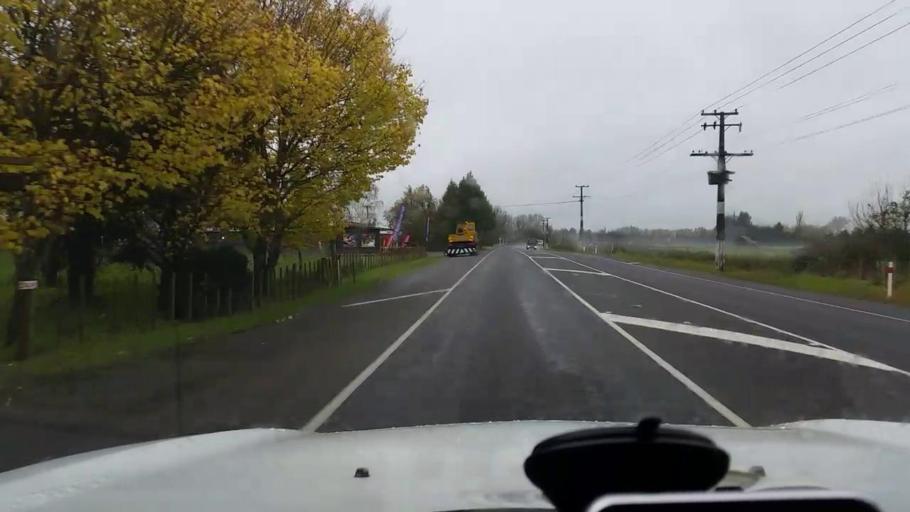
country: NZ
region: Wellington
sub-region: Masterton District
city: Masterton
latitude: -41.0703
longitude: 175.4716
